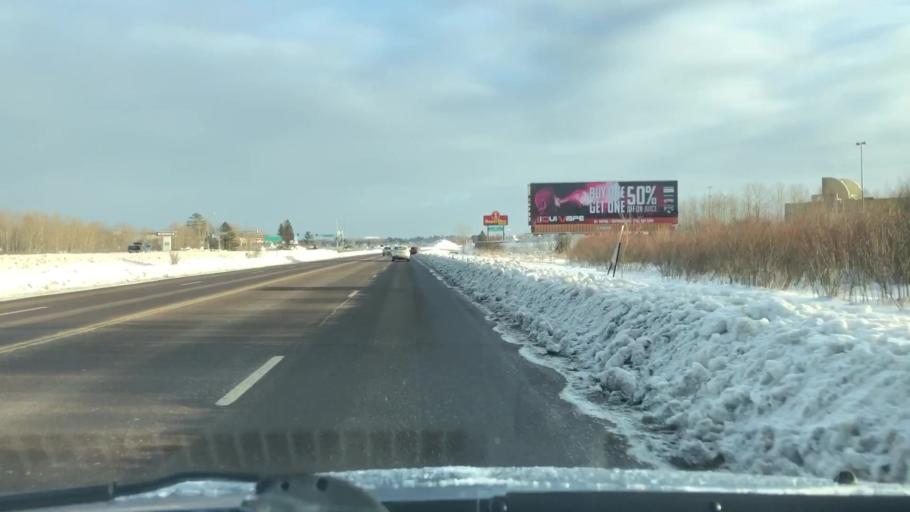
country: US
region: Minnesota
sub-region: Saint Louis County
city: Hermantown
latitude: 46.8124
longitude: -92.1718
